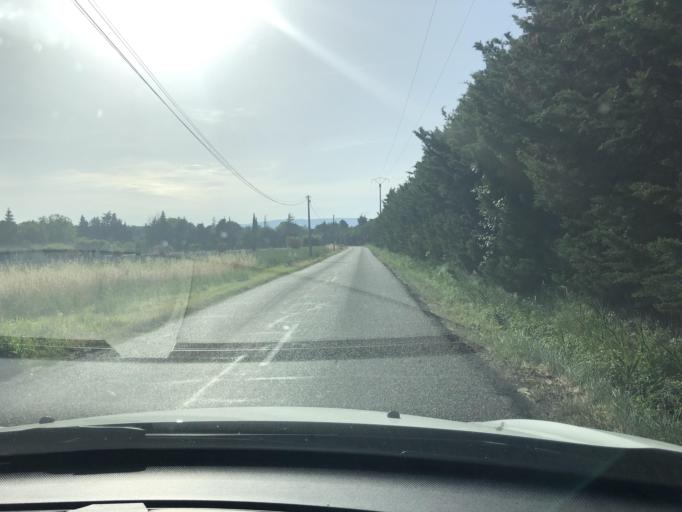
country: FR
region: Provence-Alpes-Cote d'Azur
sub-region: Departement du Vaucluse
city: Le Thor
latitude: 43.9661
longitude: 4.9897
